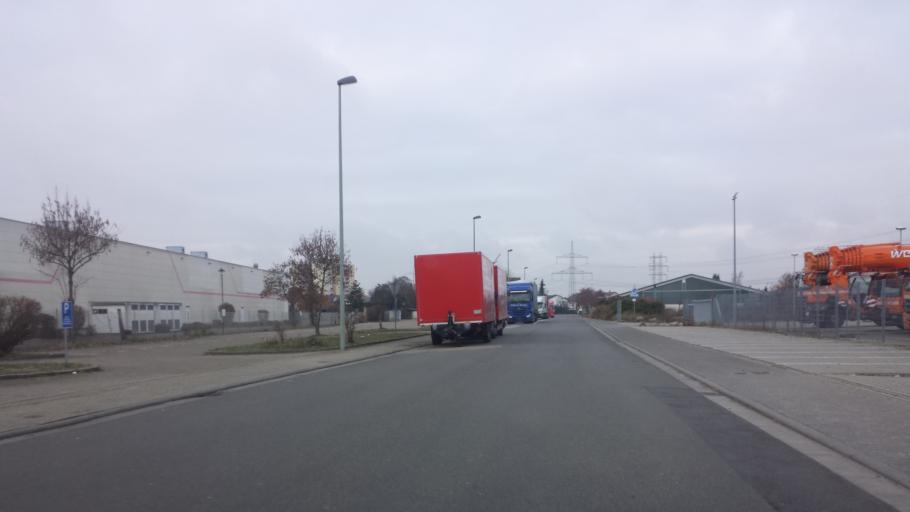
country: DE
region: Hesse
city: Lampertheim
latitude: 49.5994
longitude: 8.4824
